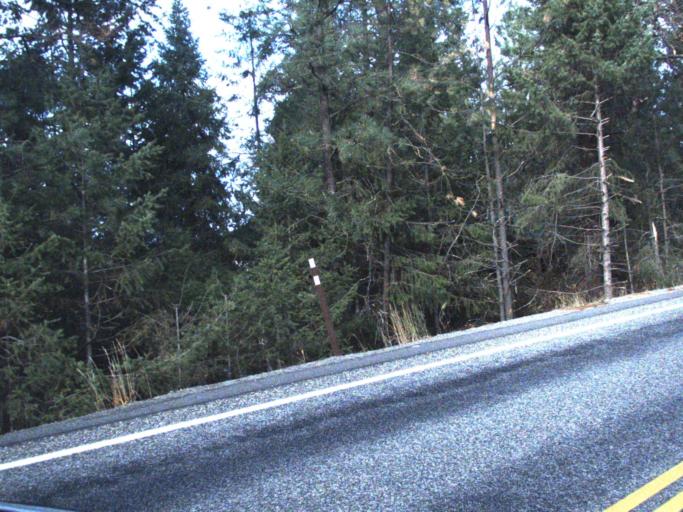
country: US
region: Washington
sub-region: Stevens County
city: Kettle Falls
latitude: 48.8138
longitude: -117.9350
